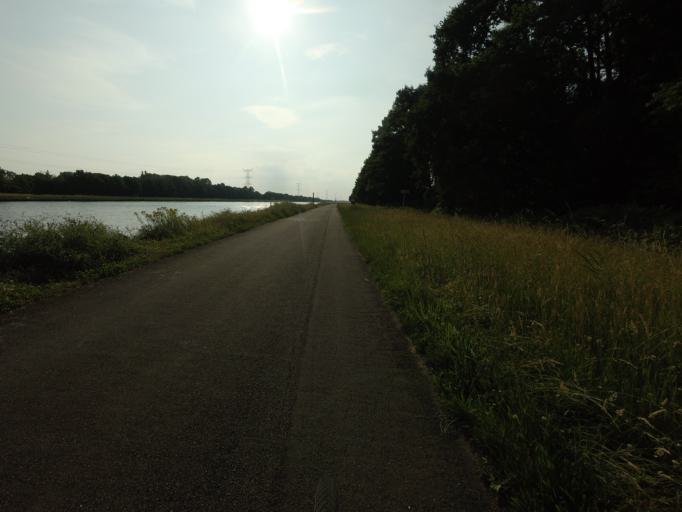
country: BE
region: Flanders
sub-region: Provincie Antwerpen
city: Nijlen
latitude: 51.1862
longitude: 4.6936
